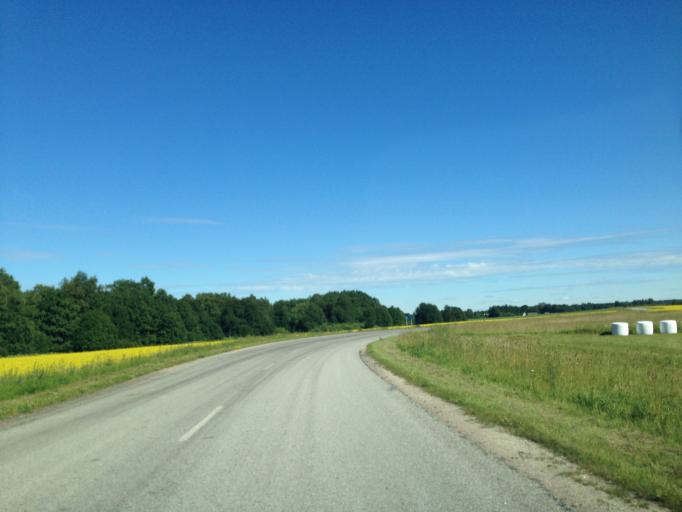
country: EE
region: Harju
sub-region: Kuusalu vald
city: Kuusalu
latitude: 59.4563
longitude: 25.3617
